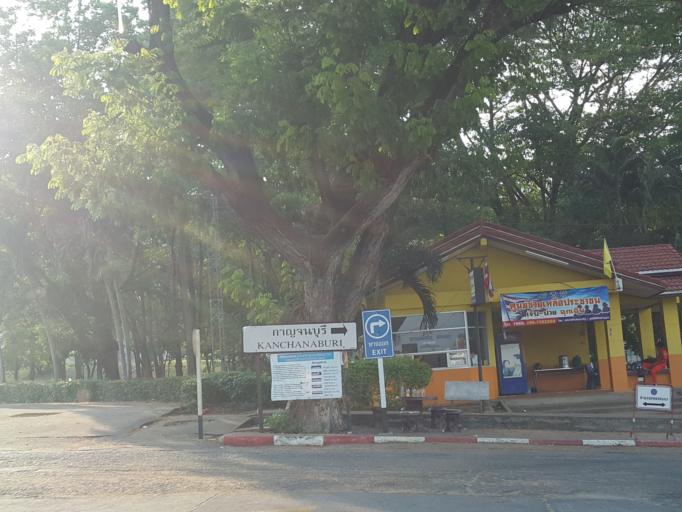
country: TH
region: Kanchanaburi
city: Si Sawat
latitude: 14.3837
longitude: 99.1357
